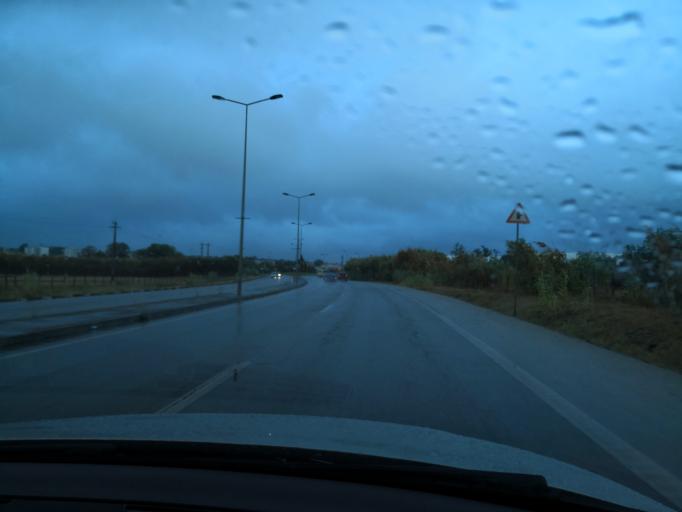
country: PT
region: Setubal
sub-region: Moita
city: Moita
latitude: 38.6509
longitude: -9.0023
